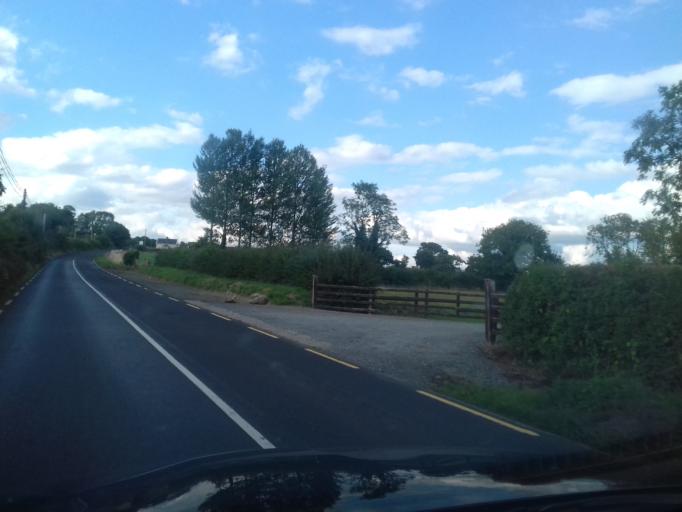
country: IE
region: Leinster
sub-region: Loch Garman
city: New Ross
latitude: 52.4379
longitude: -6.9611
